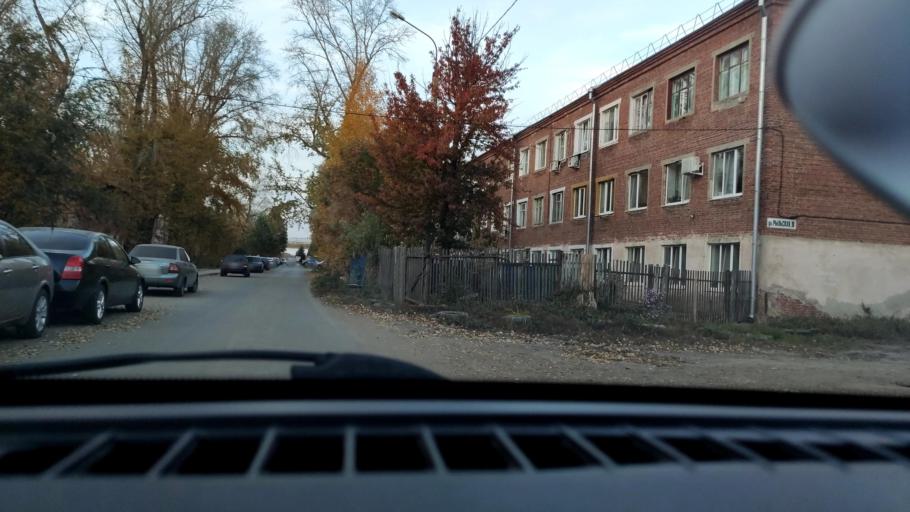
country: RU
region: Samara
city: Samara
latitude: 53.1997
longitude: 50.2497
